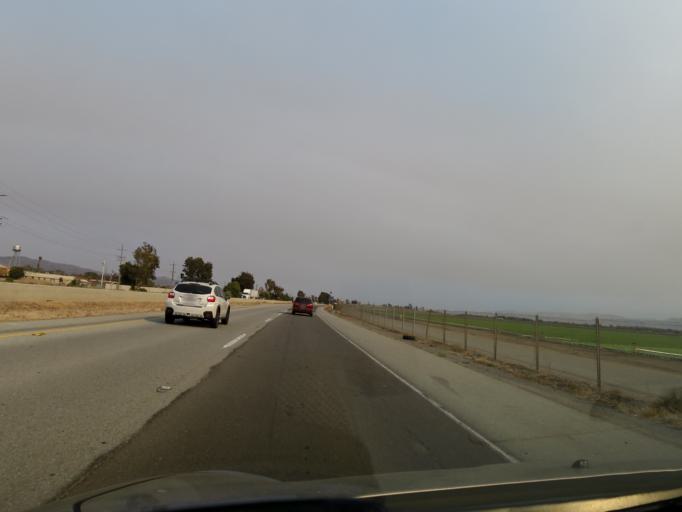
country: US
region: California
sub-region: Monterey County
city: Soledad
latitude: 36.4249
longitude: -121.3291
